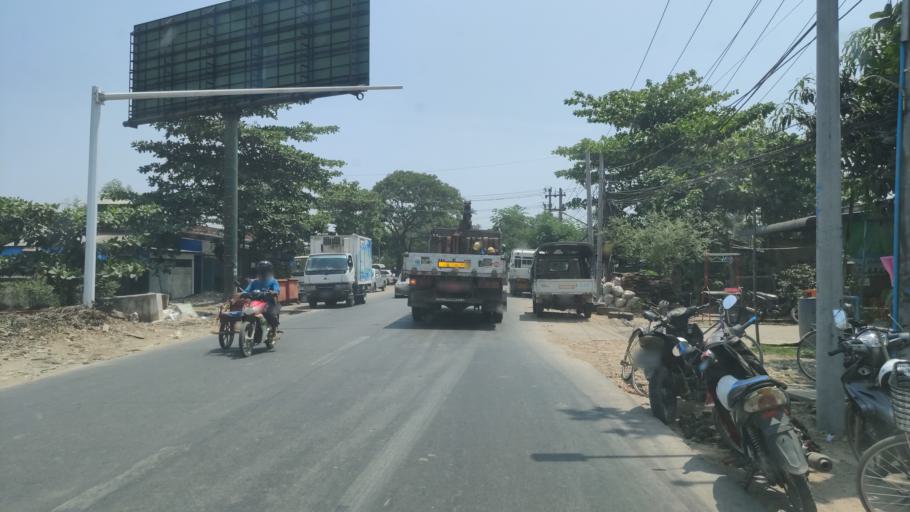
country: MM
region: Yangon
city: Yangon
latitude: 16.8940
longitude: 96.2181
